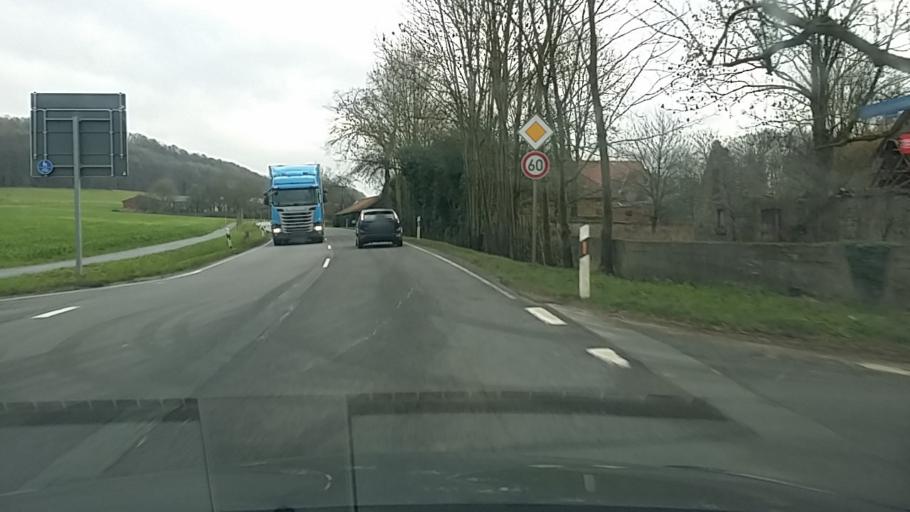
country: DE
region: North Rhine-Westphalia
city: Borgholzhausen
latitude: 52.0821
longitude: 8.2848
